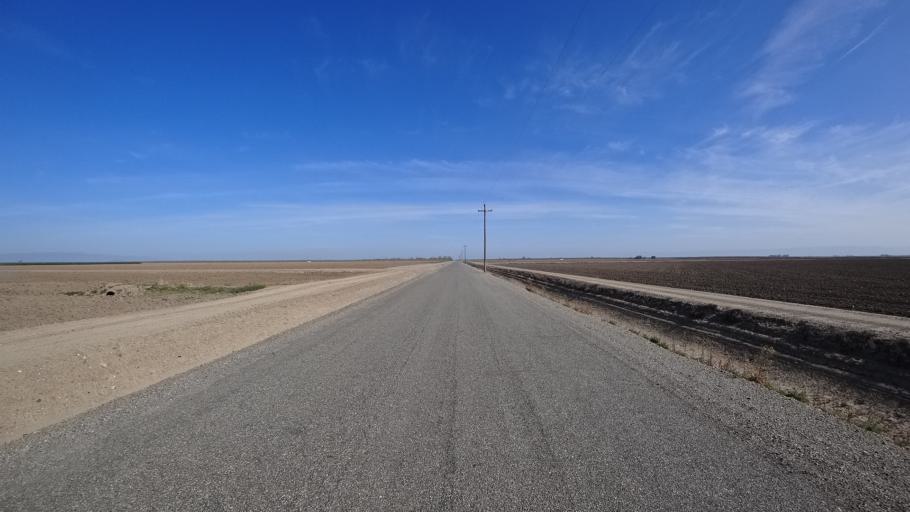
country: US
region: California
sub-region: Glenn County
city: Willows
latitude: 39.6032
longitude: -122.1169
